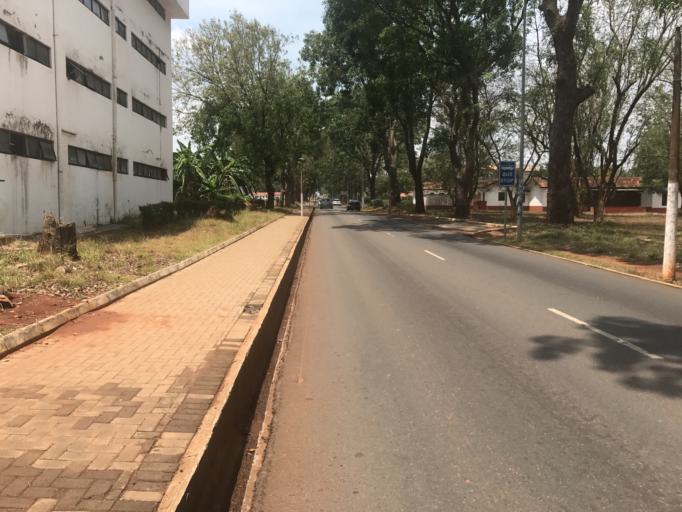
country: GH
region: Greater Accra
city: Medina Estates
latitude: 5.6471
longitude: -0.1850
